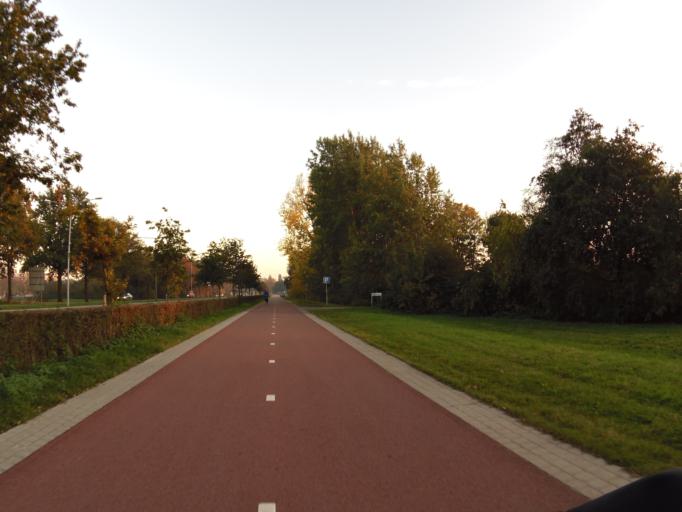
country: NL
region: North Brabant
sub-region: Gemeente 's-Hertogenbosch
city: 's-Hertogenbosch
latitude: 51.6901
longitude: 5.2652
